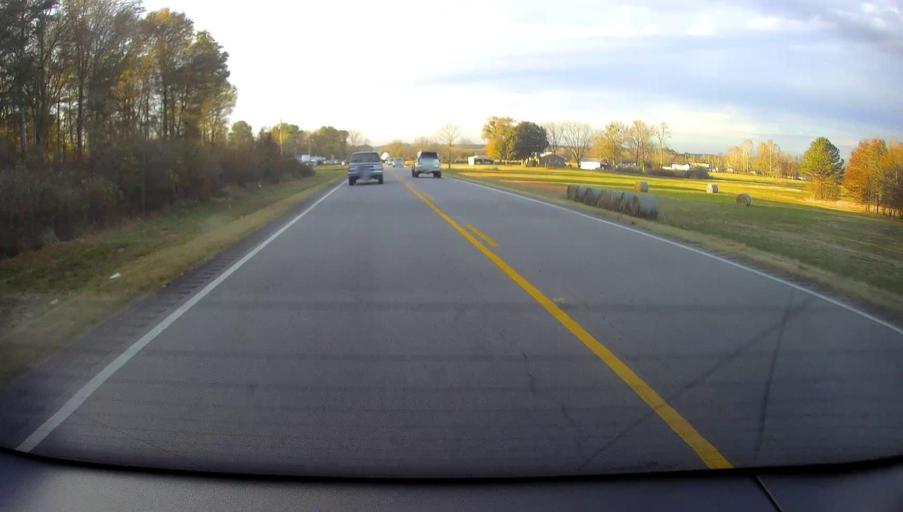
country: US
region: Alabama
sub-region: Blount County
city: Oneonta
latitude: 34.1038
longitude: -86.3707
